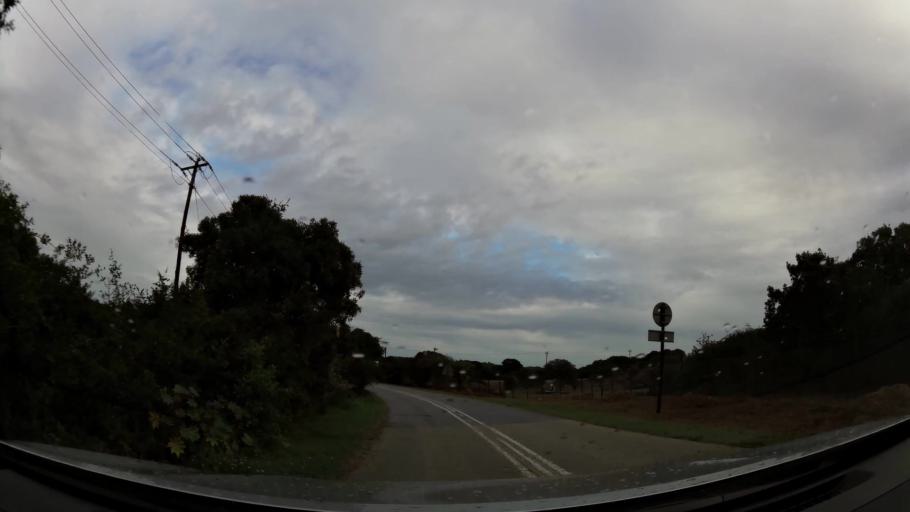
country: ZA
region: Eastern Cape
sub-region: Nelson Mandela Bay Metropolitan Municipality
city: Port Elizabeth
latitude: -34.0171
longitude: 25.4991
